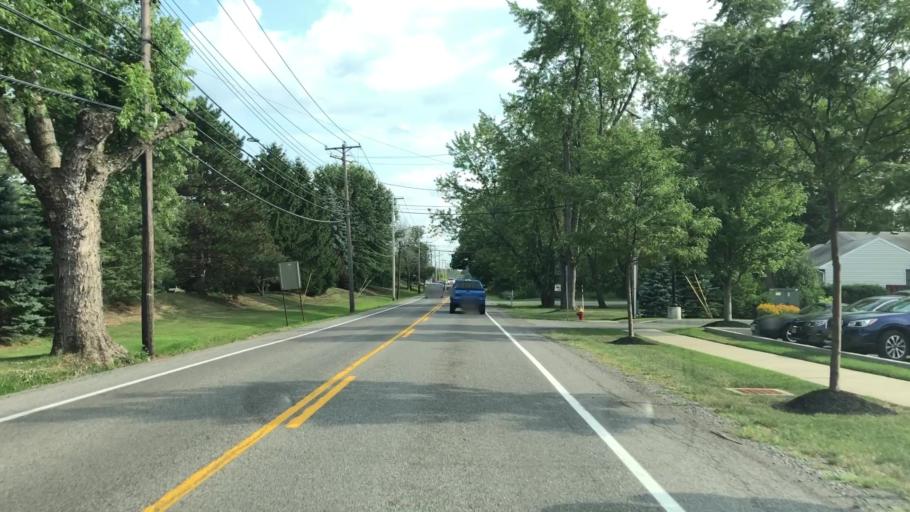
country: US
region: New York
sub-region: Erie County
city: Elma Center
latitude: 42.8381
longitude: -78.6369
